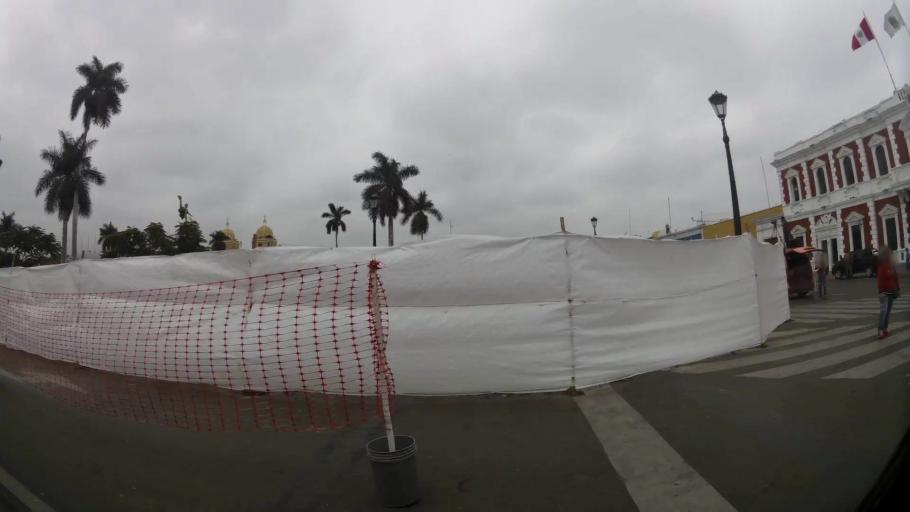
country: PE
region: La Libertad
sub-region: Provincia de Trujillo
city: Trujillo
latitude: -8.1125
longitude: -79.0287
